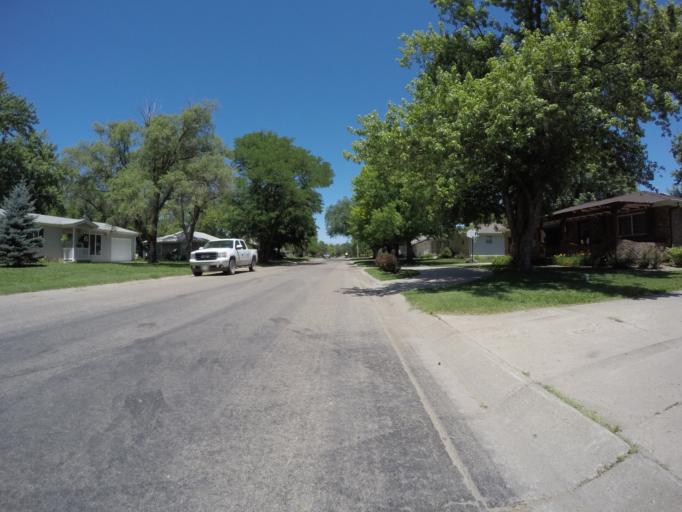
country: US
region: Kansas
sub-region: Republic County
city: Belleville
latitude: 39.8176
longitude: -97.6282
